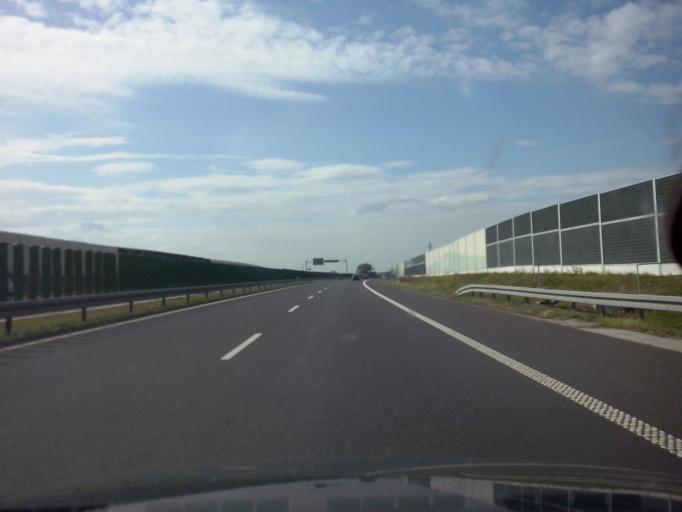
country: PL
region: Lesser Poland Voivodeship
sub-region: Powiat tarnowski
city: Tarnow
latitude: 50.0553
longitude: 21.0044
